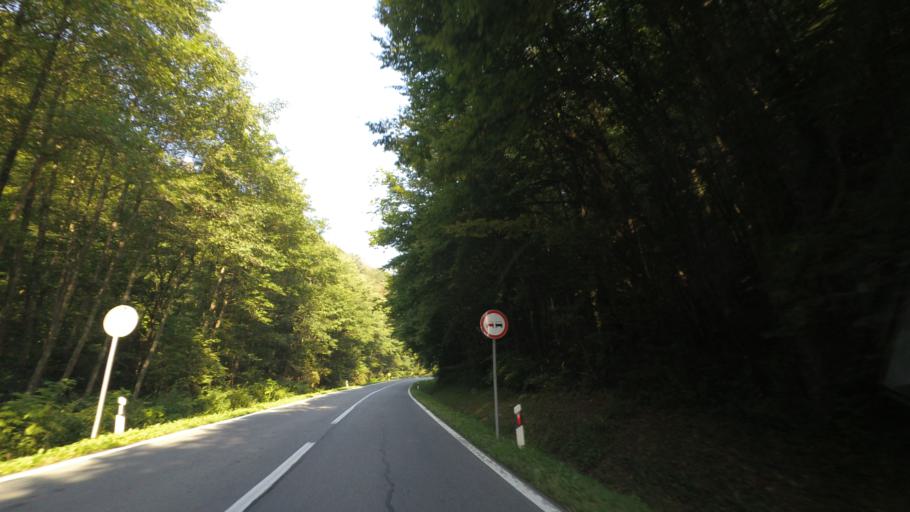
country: HR
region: Brodsko-Posavska
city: Cernik
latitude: 45.4532
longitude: 17.4624
